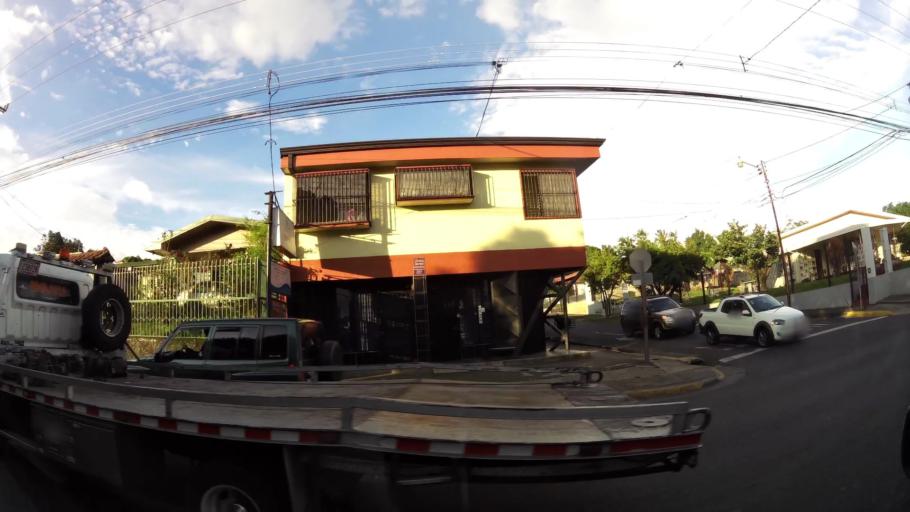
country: CR
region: Heredia
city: Llorente
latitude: 10.0007
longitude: -84.1516
